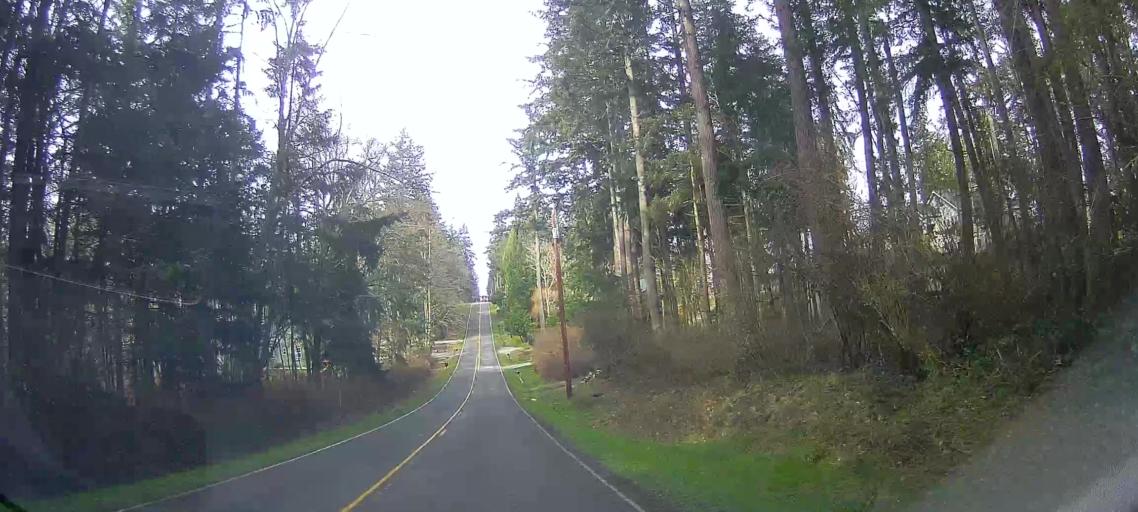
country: US
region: Washington
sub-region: Island County
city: Langley
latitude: 48.0642
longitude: -122.3664
